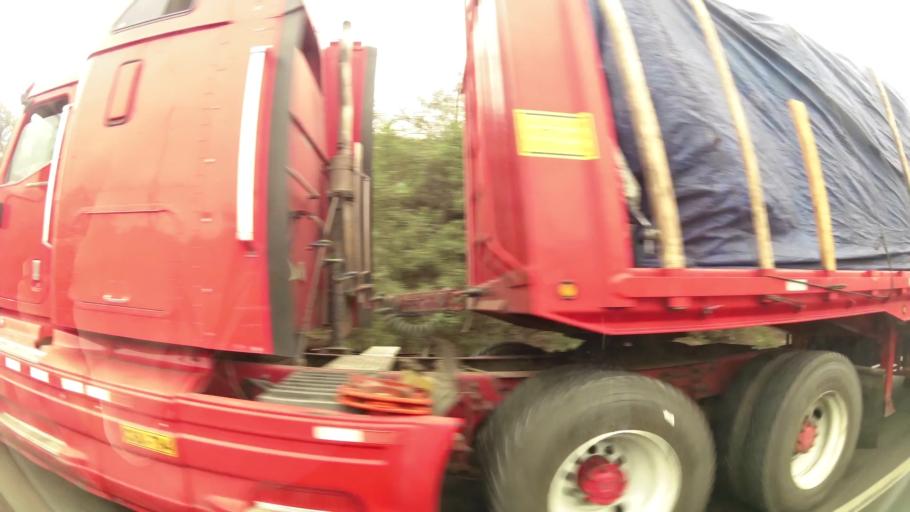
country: PE
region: Lima
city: Ventanilla
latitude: -11.8226
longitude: -77.1249
